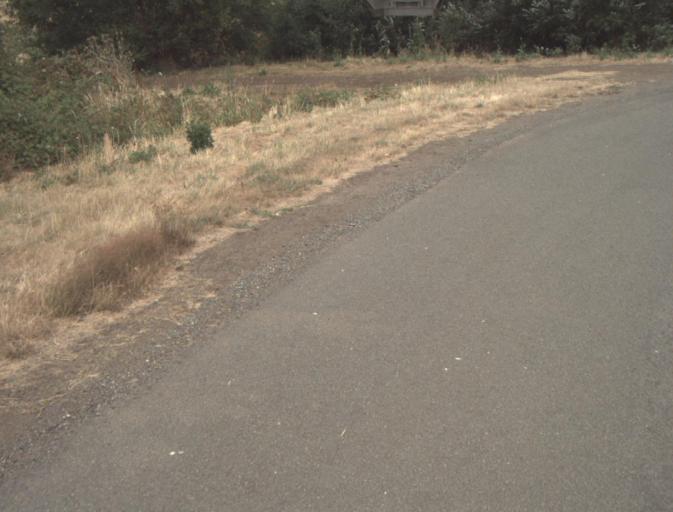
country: AU
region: Tasmania
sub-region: Launceston
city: Newstead
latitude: -41.4348
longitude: 147.1806
